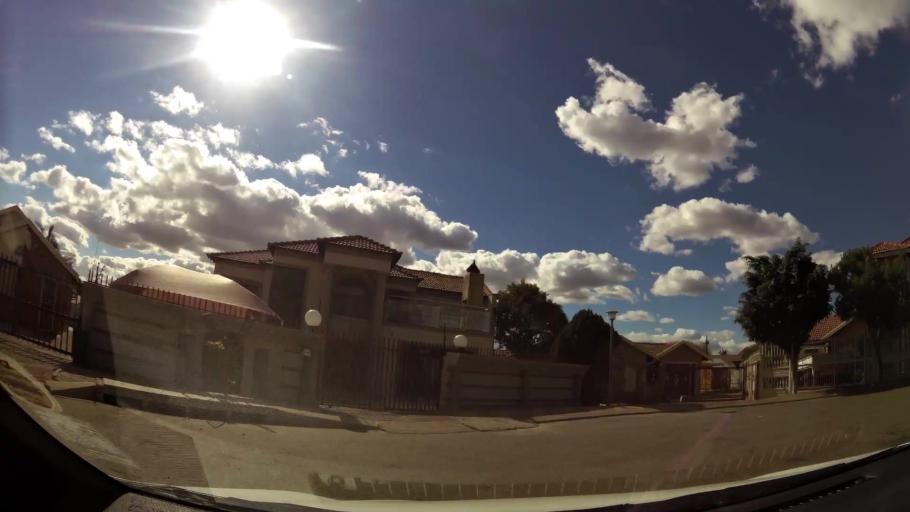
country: ZA
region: Limpopo
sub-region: Capricorn District Municipality
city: Polokwane
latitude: -23.8843
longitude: 29.4716
